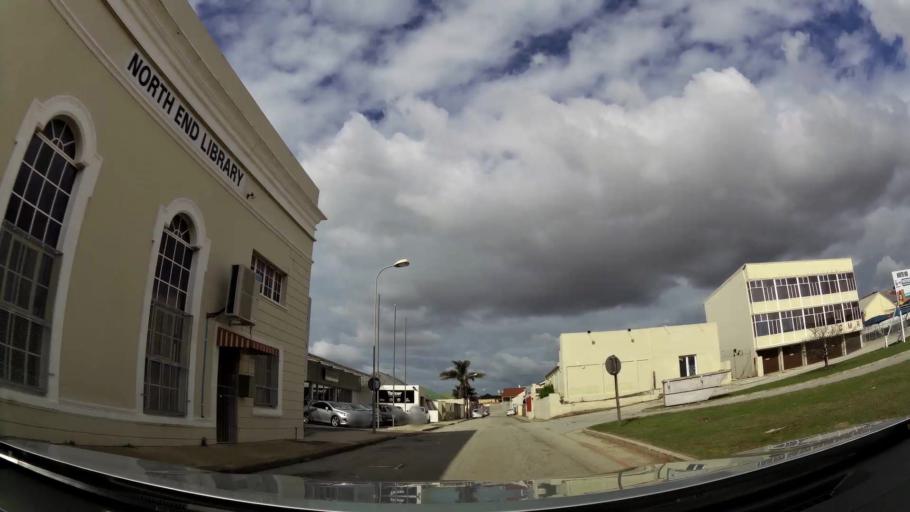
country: ZA
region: Eastern Cape
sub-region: Nelson Mandela Bay Metropolitan Municipality
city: Port Elizabeth
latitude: -33.9476
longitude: 25.6033
